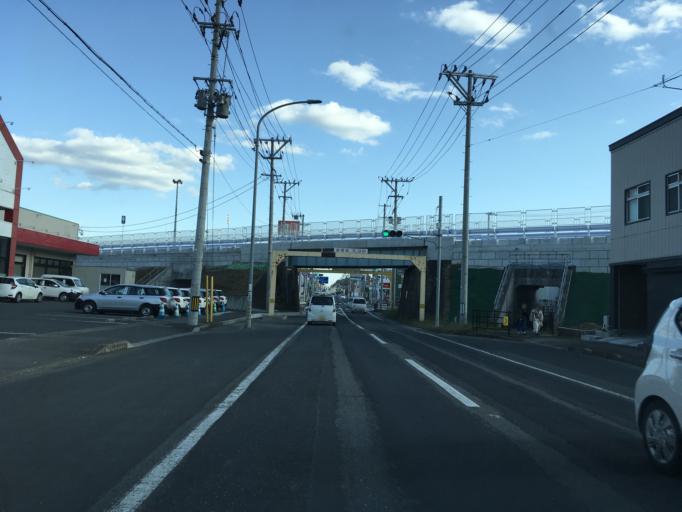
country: JP
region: Iwate
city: Ofunato
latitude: 38.8980
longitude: 141.5655
